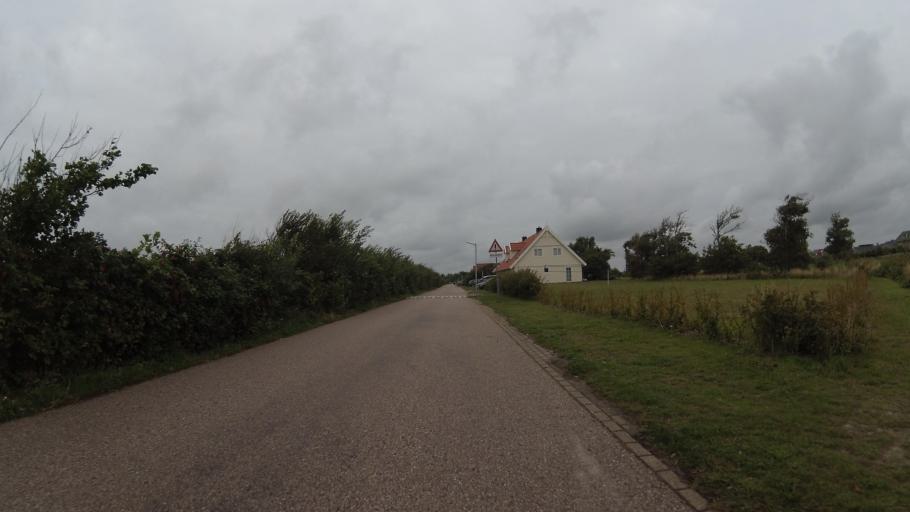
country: NL
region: North Holland
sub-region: Gemeente Den Helder
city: Den Helder
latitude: 52.8848
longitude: 4.7267
